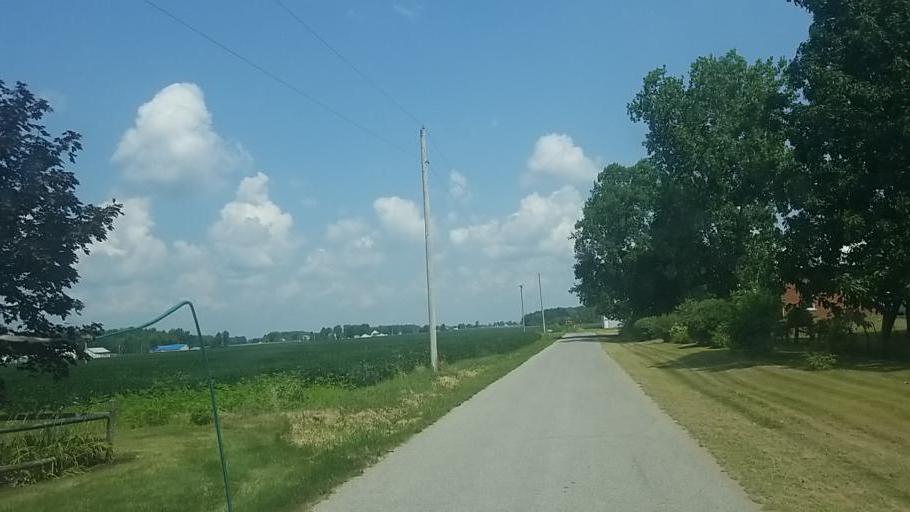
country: US
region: Ohio
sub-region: Crawford County
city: Crestline
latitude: 40.8070
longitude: -82.7259
